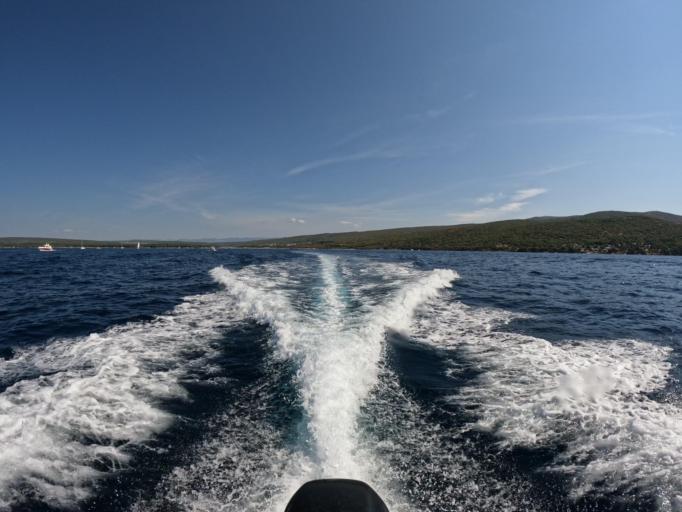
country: HR
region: Primorsko-Goranska
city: Punat
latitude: 44.9937
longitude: 14.6165
